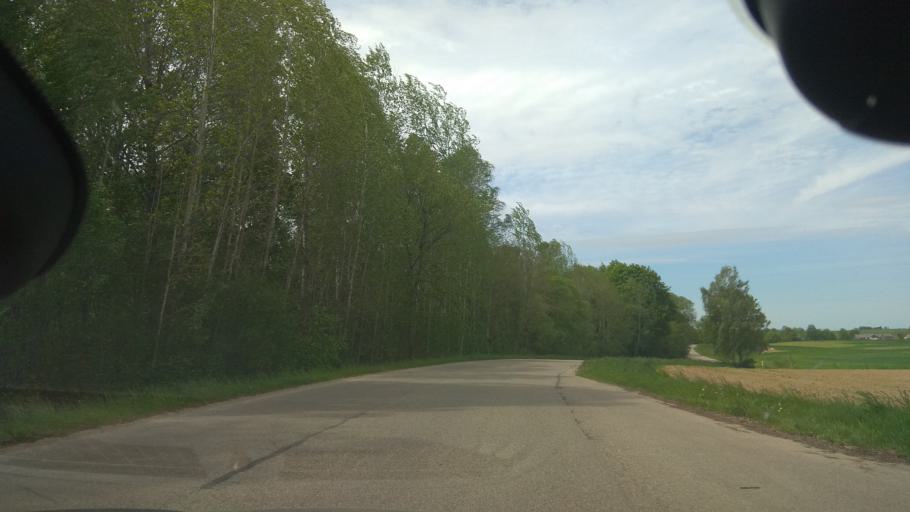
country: LT
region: Vilnius County
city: Ukmerge
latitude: 55.1508
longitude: 24.5514
